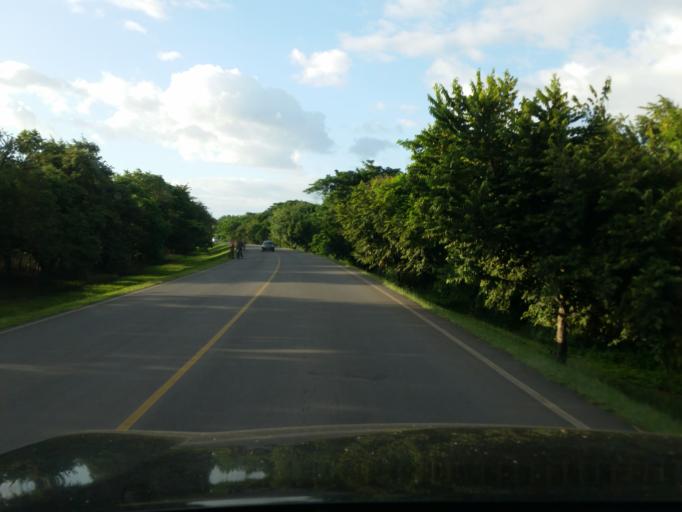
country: NI
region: Granada
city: Nandaime
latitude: 11.7452
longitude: -86.0254
